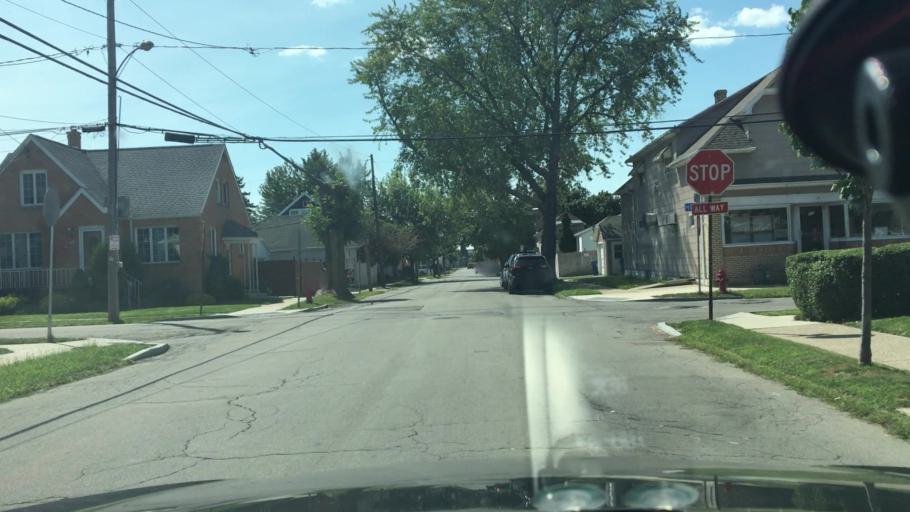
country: US
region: New York
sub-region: Erie County
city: West Seneca
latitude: 42.8687
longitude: -78.8038
